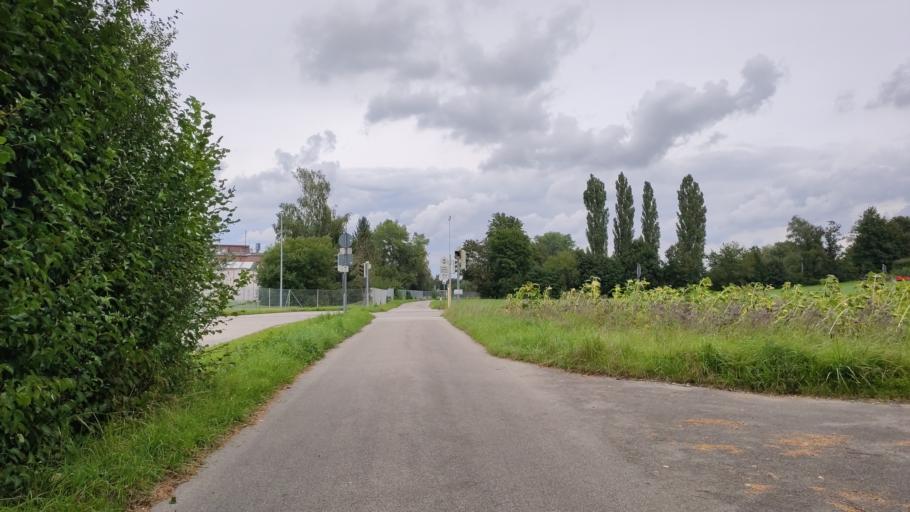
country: DE
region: Bavaria
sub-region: Swabia
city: Wehringen
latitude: 48.2600
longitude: 10.8145
